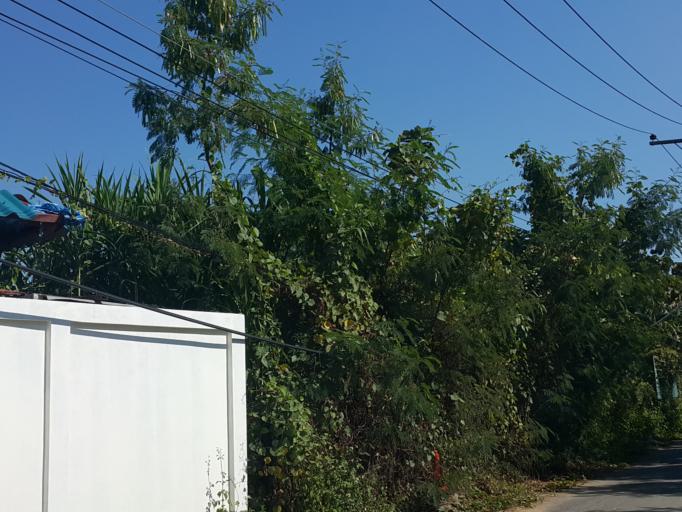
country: TH
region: Chiang Mai
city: San Sai
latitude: 18.8873
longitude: 98.9889
